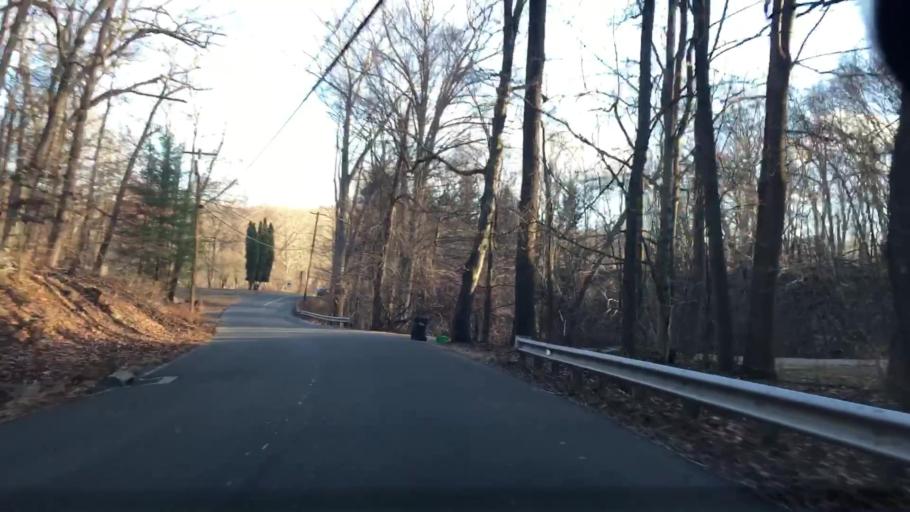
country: US
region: Connecticut
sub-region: Fairfield County
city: Newtown
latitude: 41.4429
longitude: -73.3176
